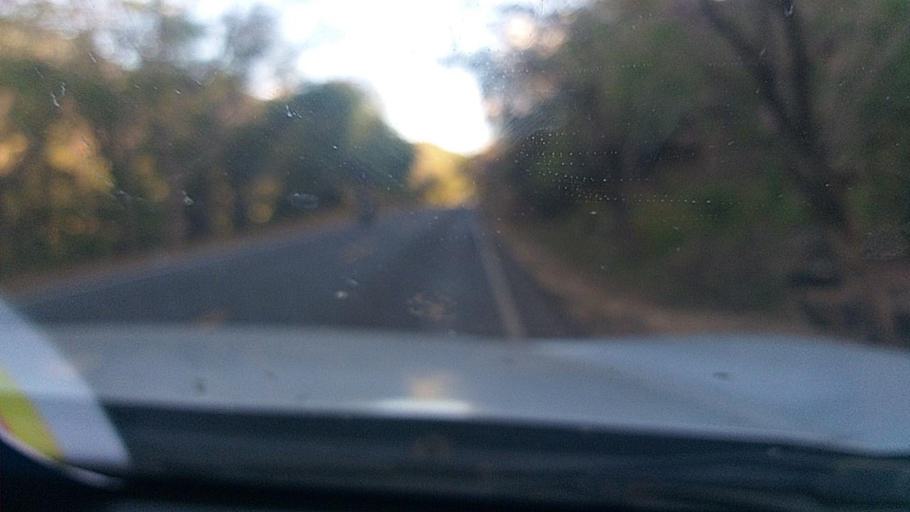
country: NI
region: Esteli
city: Condega
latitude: 13.2967
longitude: -86.3488
